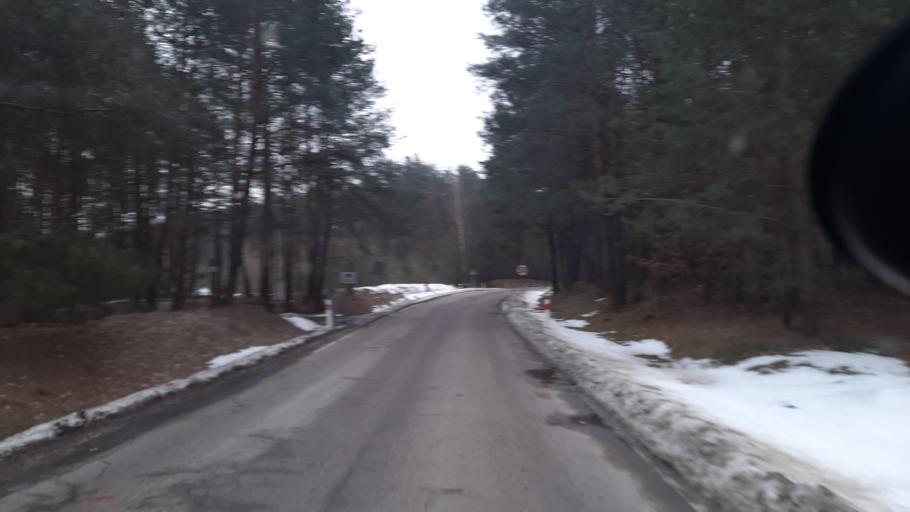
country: PL
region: Lublin Voivodeship
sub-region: Powiat wlodawski
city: Wlodawa
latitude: 51.4920
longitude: 23.5898
